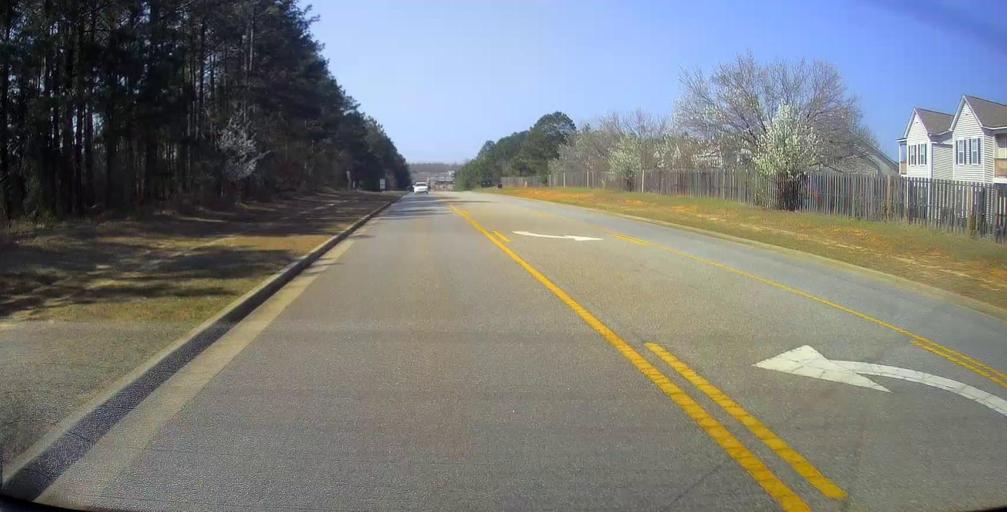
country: US
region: Georgia
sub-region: Houston County
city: Centerville
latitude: 32.6123
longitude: -83.7075
